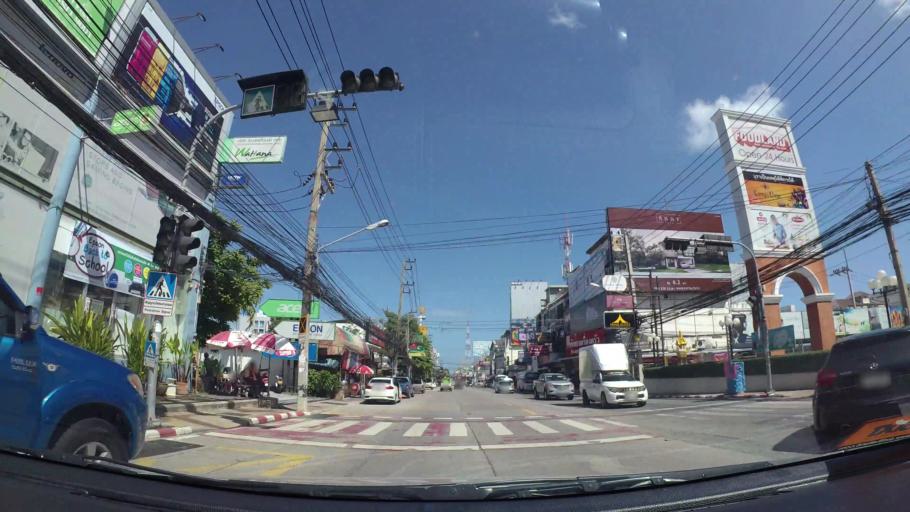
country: TH
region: Chon Buri
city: Phatthaya
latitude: 12.9331
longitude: 100.8970
